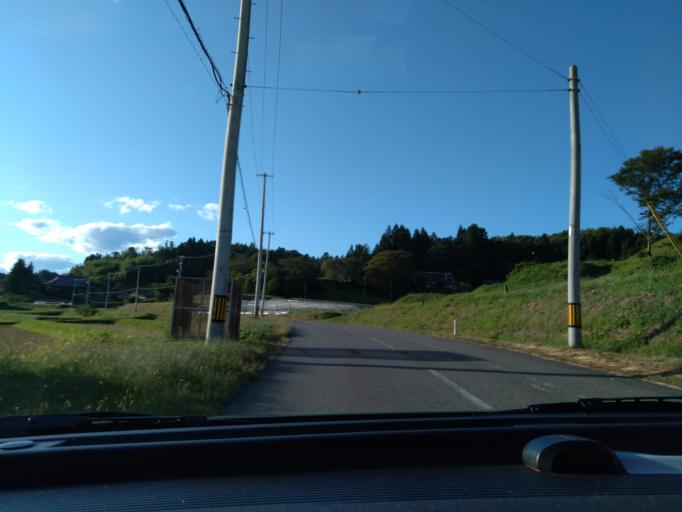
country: JP
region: Iwate
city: Ichinoseki
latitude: 38.8675
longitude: 141.1870
